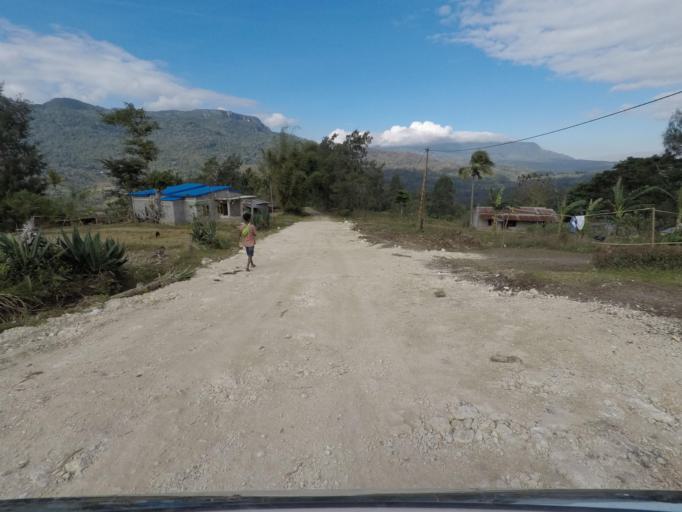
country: TL
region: Baucau
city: Venilale
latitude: -8.6504
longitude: 126.3924
